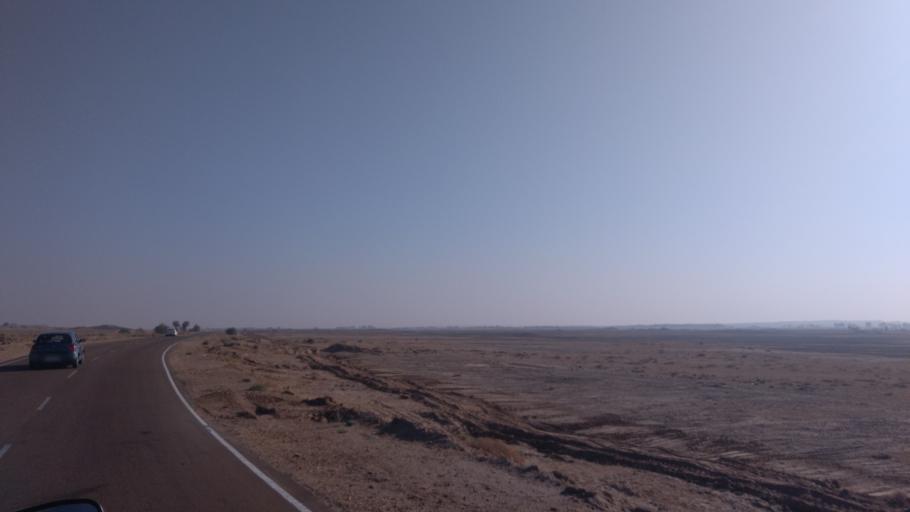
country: IN
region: Rajasthan
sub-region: Jaisalmer
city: Jaisalmer
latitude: 26.8857
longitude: 70.6667
